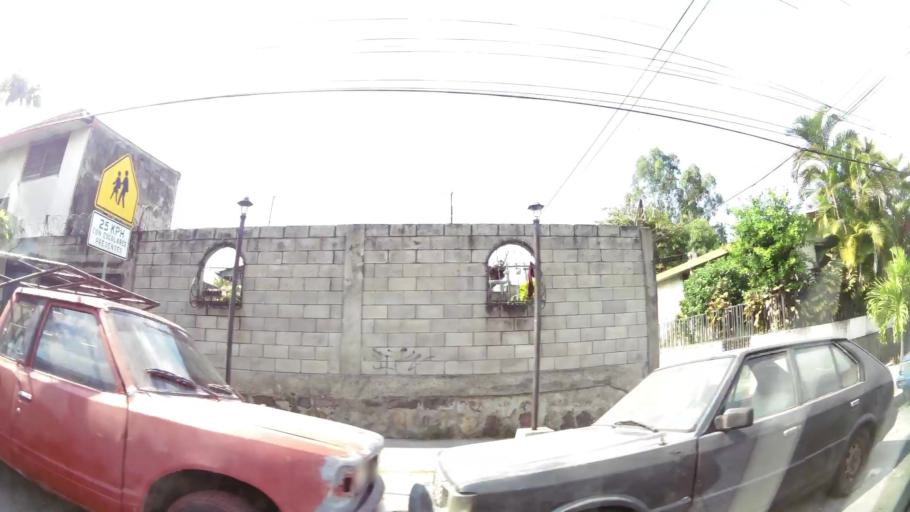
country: SV
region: San Salvador
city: Mejicanos
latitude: 13.7235
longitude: -89.2115
